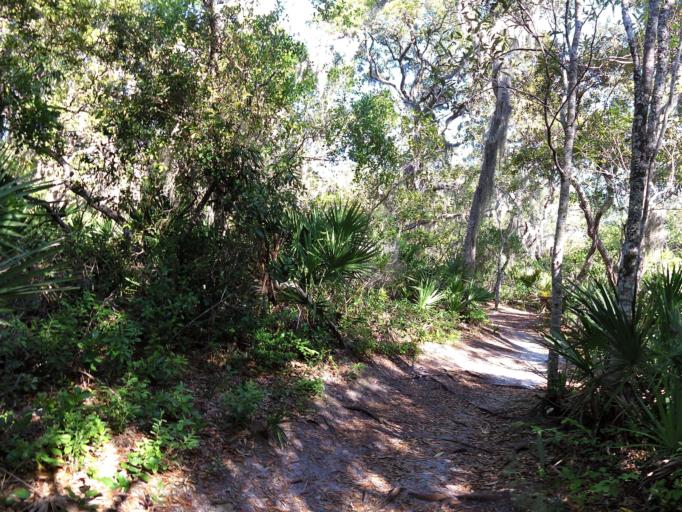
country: US
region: Florida
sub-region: Duval County
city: Atlantic Beach
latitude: 30.3820
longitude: -81.4883
